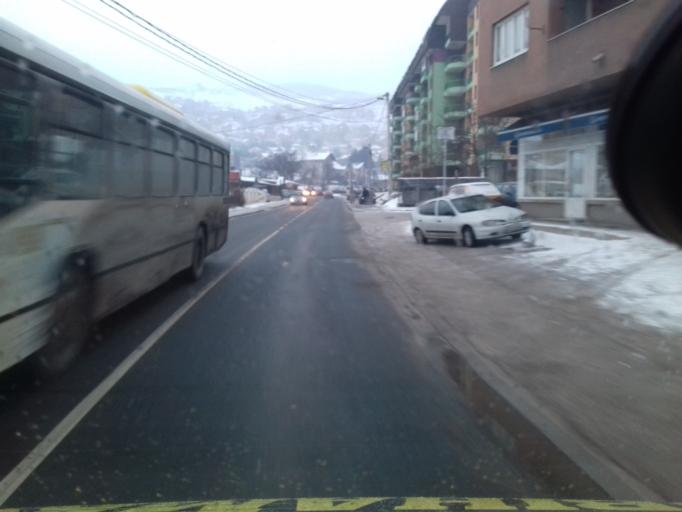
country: BA
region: Federation of Bosnia and Herzegovina
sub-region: Kanton Sarajevo
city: Sarajevo
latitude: 43.8567
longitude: 18.3659
